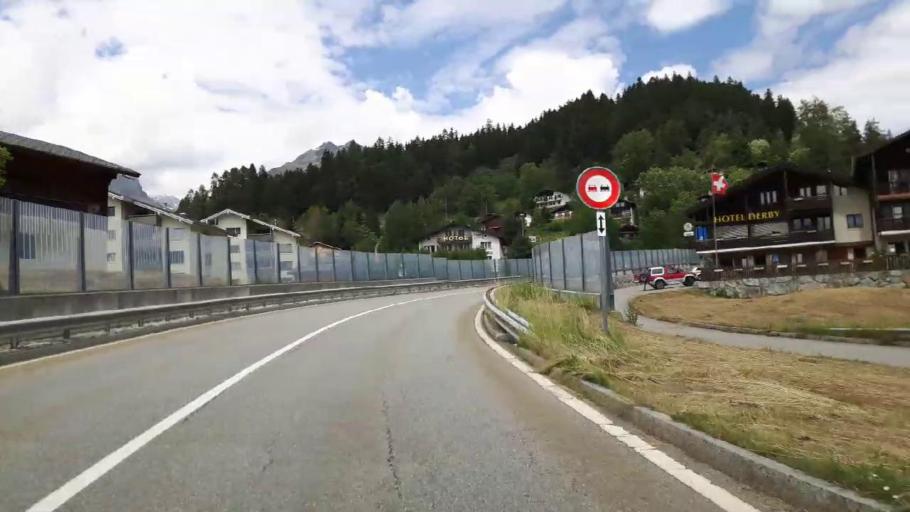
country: CH
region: Valais
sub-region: Goms District
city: Fiesch
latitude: 46.4008
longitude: 8.1373
